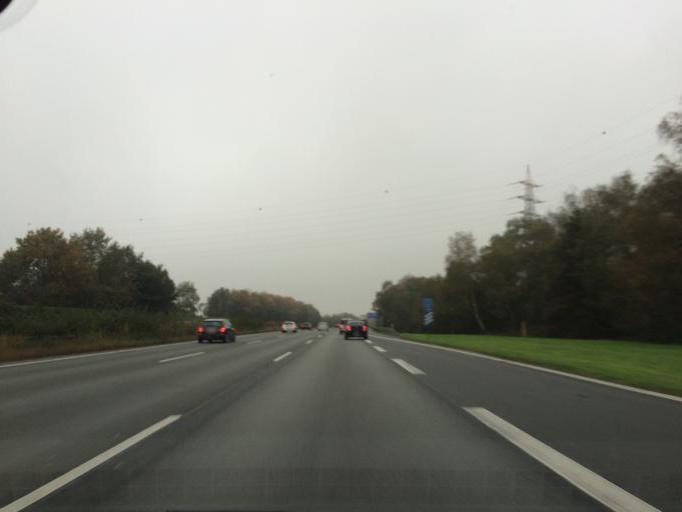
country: DE
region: North Rhine-Westphalia
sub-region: Regierungsbezirk Munster
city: Bottrop
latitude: 51.5399
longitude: 6.8810
